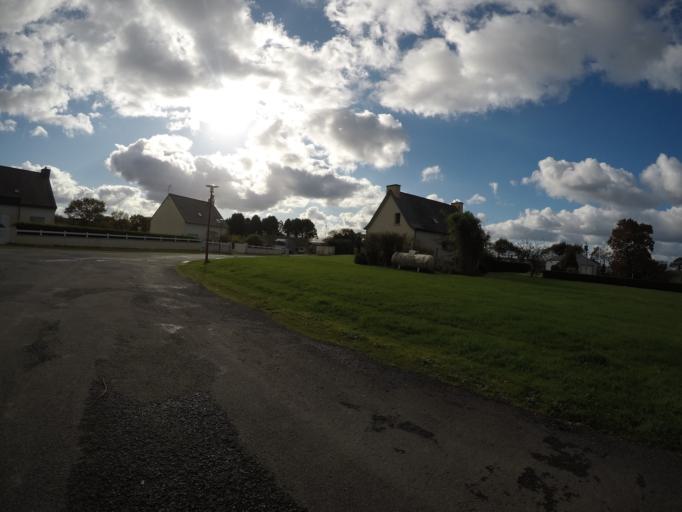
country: FR
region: Brittany
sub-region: Departement des Cotes-d'Armor
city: Louargat
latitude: 48.4641
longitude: -3.3066
